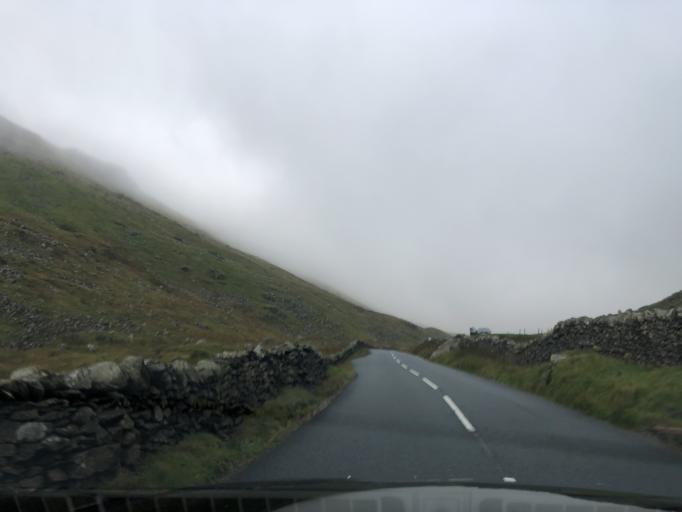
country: GB
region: England
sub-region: Cumbria
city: Ambleside
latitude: 54.4731
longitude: -2.9230
